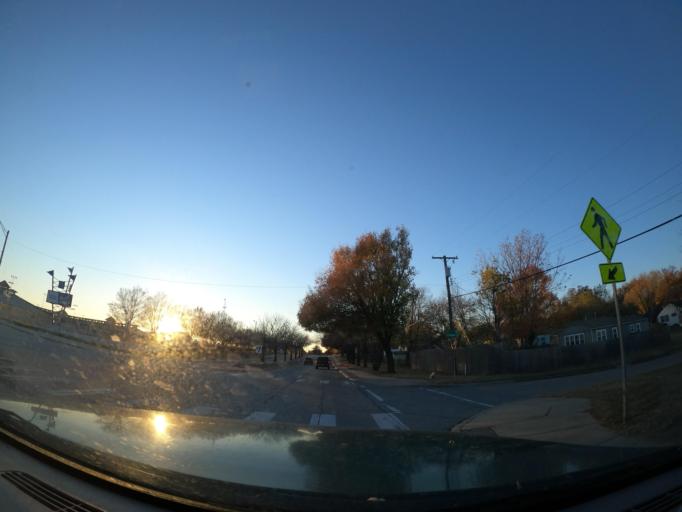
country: US
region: Oklahoma
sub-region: Tulsa County
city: Tulsa
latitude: 36.1406
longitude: -95.9258
